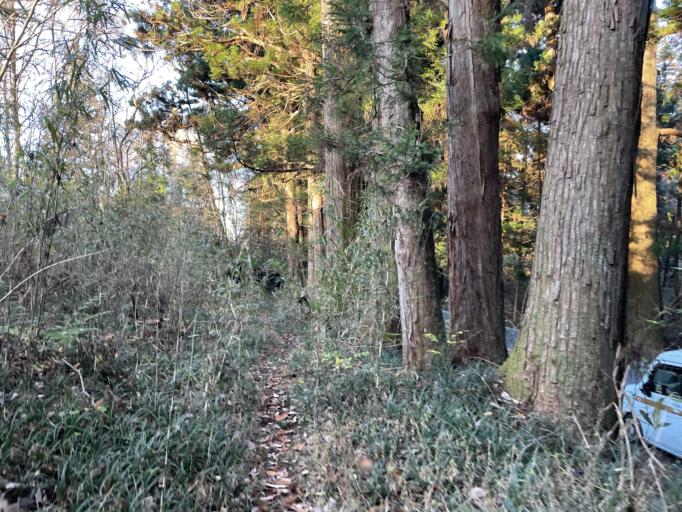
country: JP
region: Tochigi
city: Imaichi
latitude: 36.6668
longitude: 139.7214
